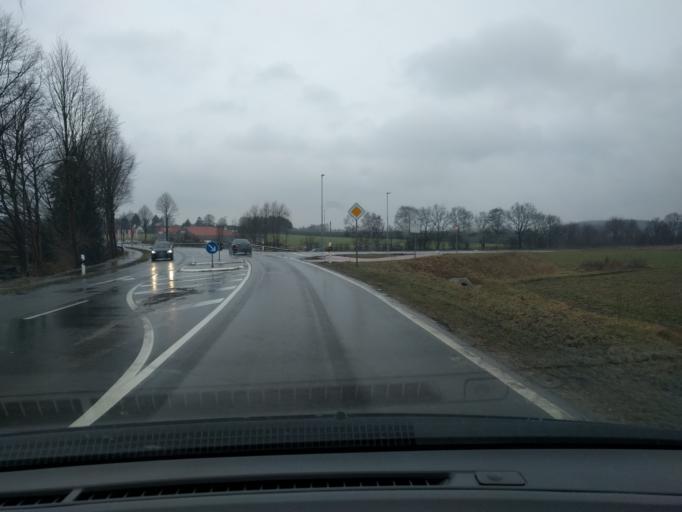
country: DE
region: Lower Saxony
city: Bendestorf
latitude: 53.3666
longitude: 9.9318
